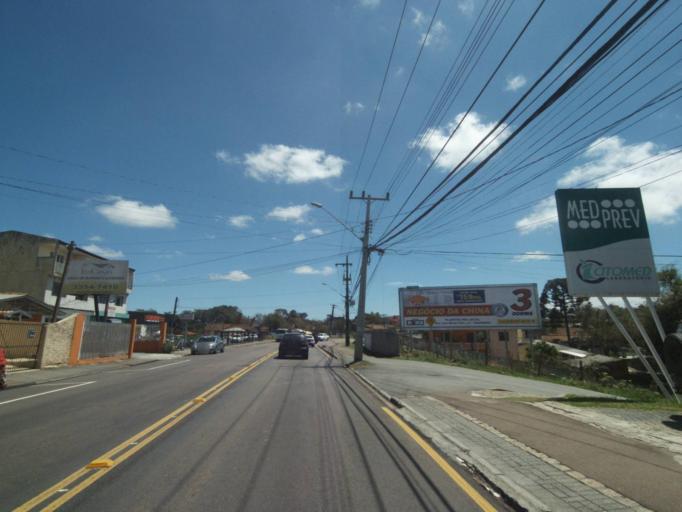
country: BR
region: Parana
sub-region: Curitiba
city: Curitiba
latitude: -25.3797
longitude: -49.2620
